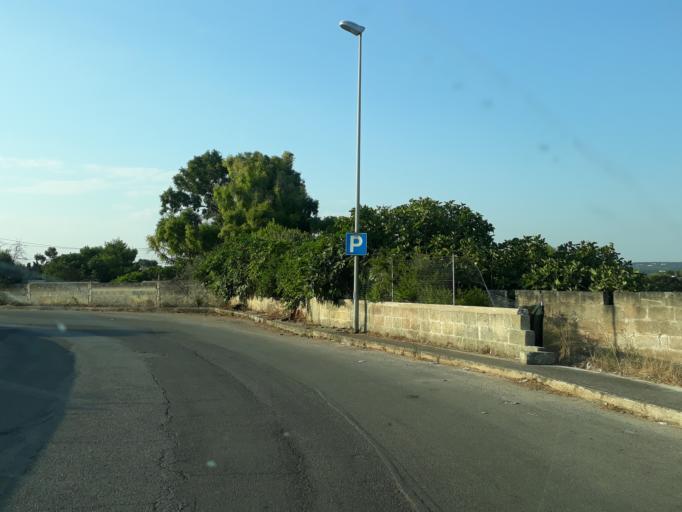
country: IT
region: Apulia
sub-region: Provincia di Brindisi
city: Carovigno
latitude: 40.7548
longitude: 17.7043
